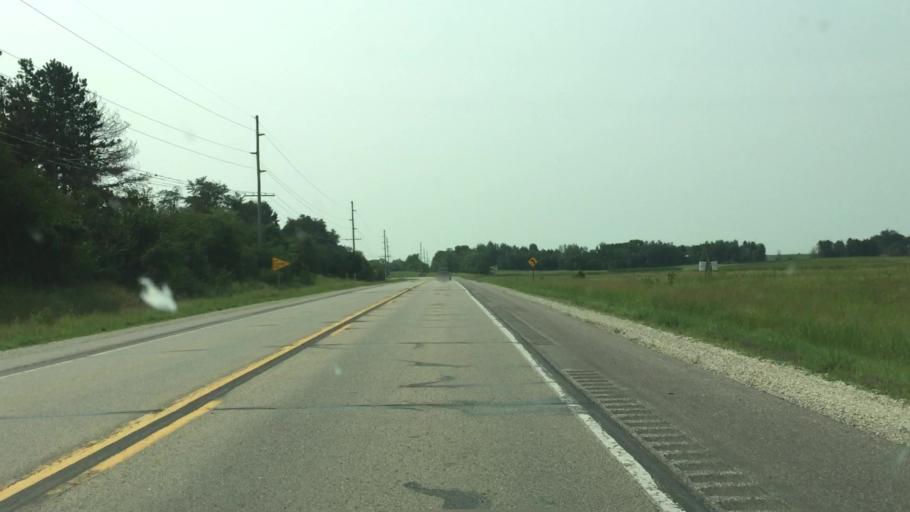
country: US
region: Iowa
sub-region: Dickinson County
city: Milford
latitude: 43.3494
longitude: -95.1798
